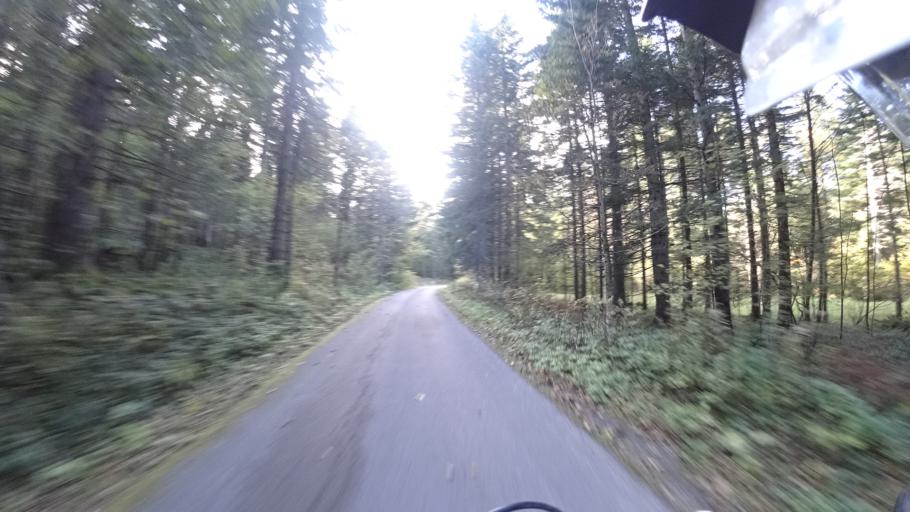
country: HR
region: Karlovacka
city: Plaski
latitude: 44.9820
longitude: 15.4080
